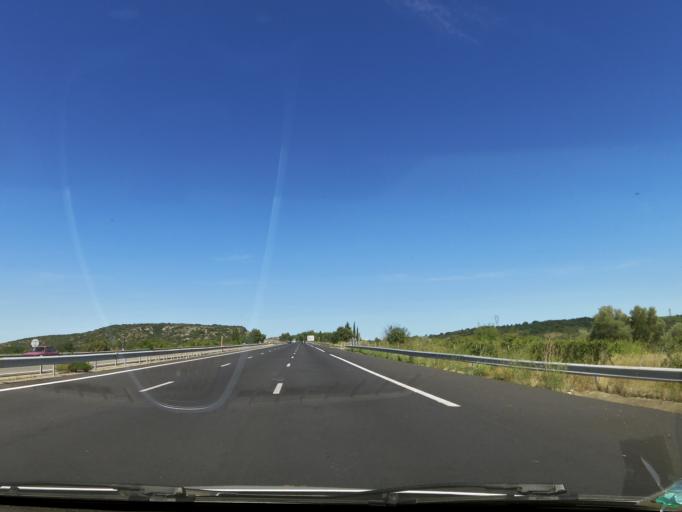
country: FR
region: Languedoc-Roussillon
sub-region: Departement du Gard
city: Remoulins
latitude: 43.9363
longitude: 4.6032
